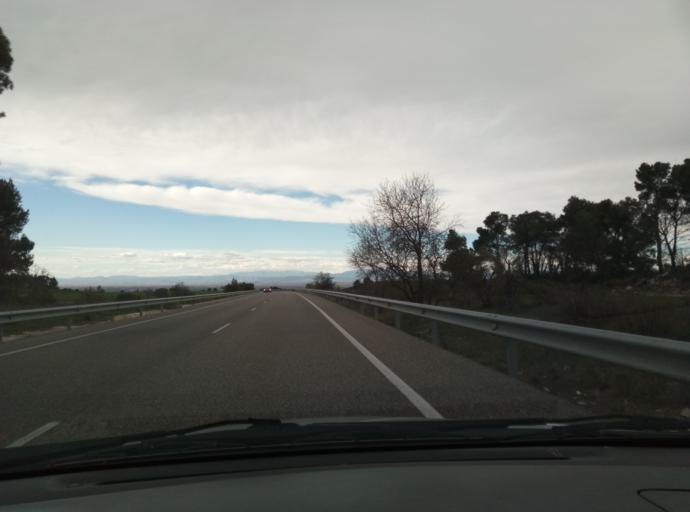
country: ES
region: Catalonia
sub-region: Provincia de Lleida
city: Ciutadilla
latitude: 41.5387
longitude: 1.1493
